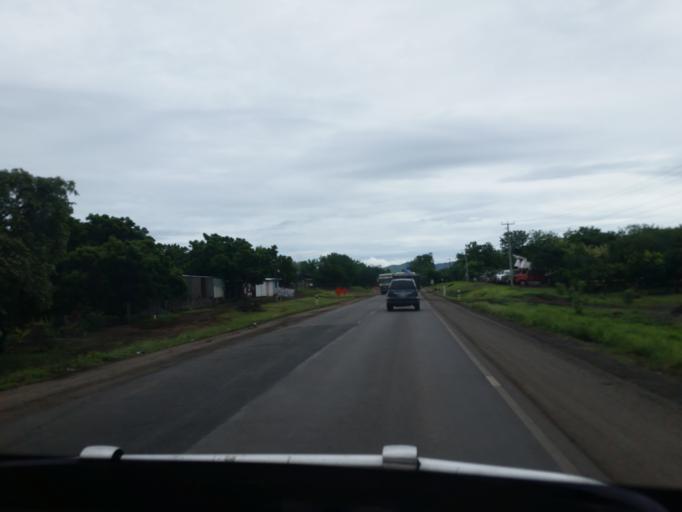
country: NI
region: Managua
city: Tipitapa
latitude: 12.2835
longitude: -86.0618
